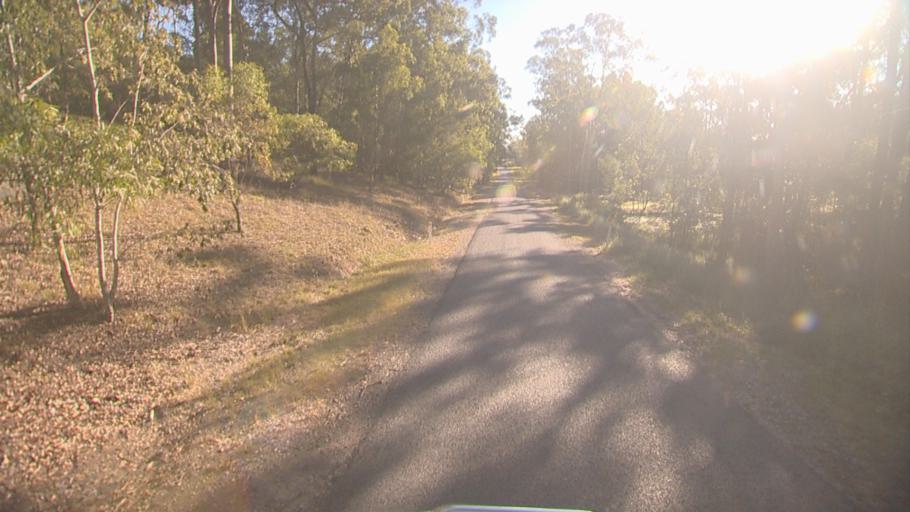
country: AU
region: Queensland
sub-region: Logan
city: Windaroo
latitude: -27.7723
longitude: 153.1498
